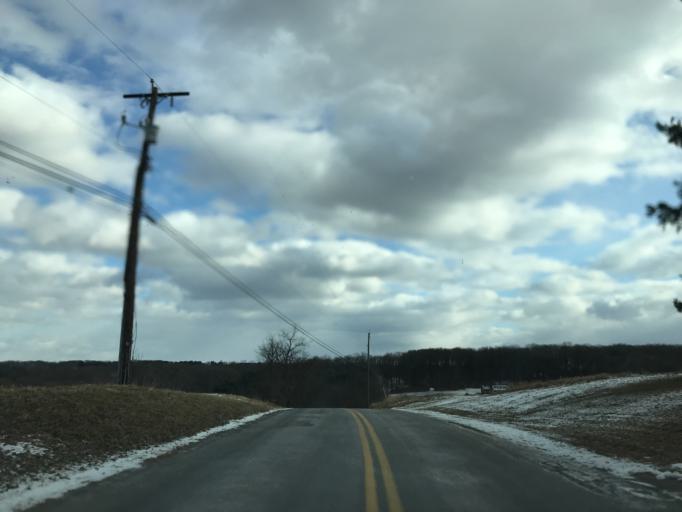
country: US
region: Maryland
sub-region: Harford County
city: Jarrettsville
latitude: 39.6314
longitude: -76.4860
